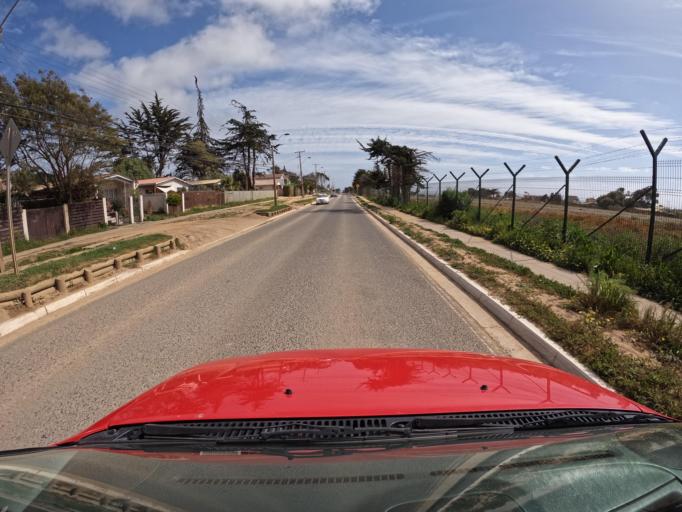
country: CL
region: O'Higgins
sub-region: Provincia de Colchagua
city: Santa Cruz
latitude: -34.3966
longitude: -72.0196
